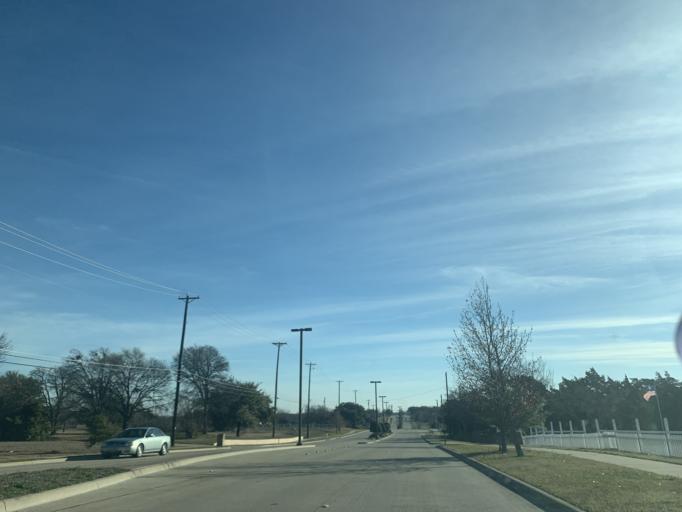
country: US
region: Texas
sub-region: Dallas County
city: DeSoto
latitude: 32.5751
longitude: -96.8351
